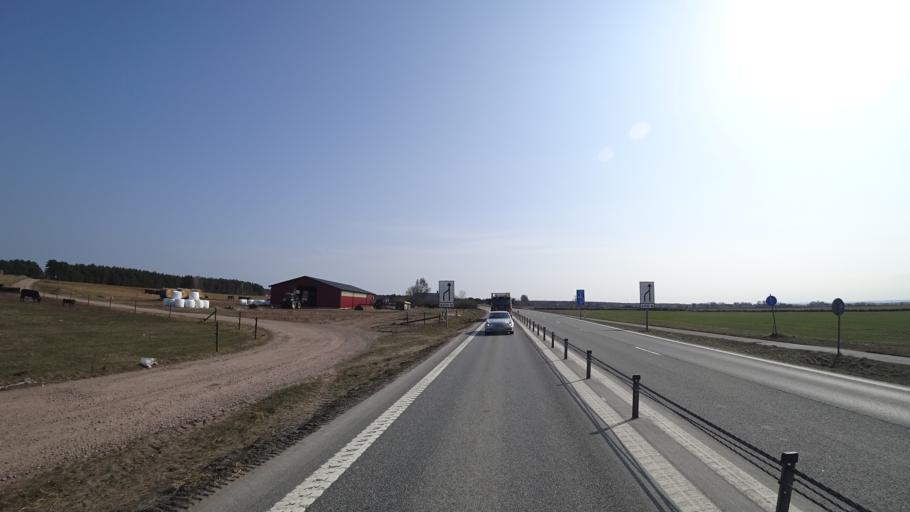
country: SE
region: Skane
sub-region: Kristianstads Kommun
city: Ahus
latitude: 55.9720
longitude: 14.2739
